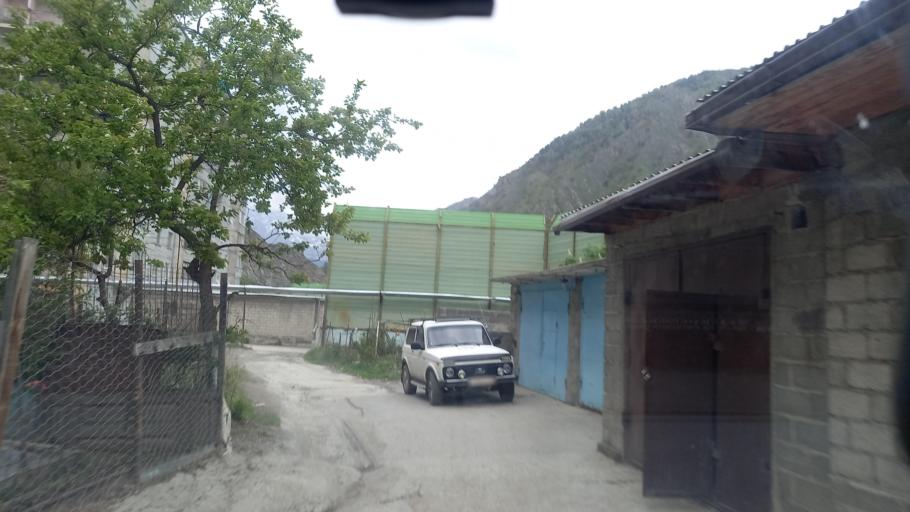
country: RU
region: North Ossetia
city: Mizur
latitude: 42.8522
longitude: 44.0687
